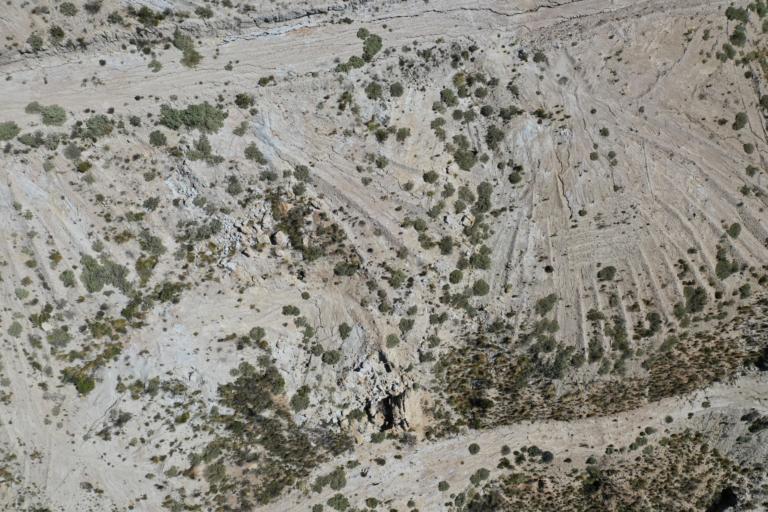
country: BO
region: La Paz
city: La Paz
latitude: -16.5563
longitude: -68.1226
